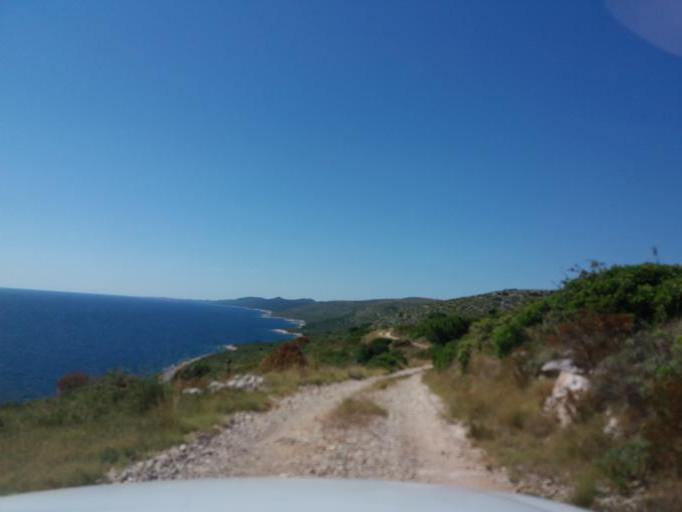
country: HR
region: Zadarska
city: Ugljan
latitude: 44.0131
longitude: 15.0302
